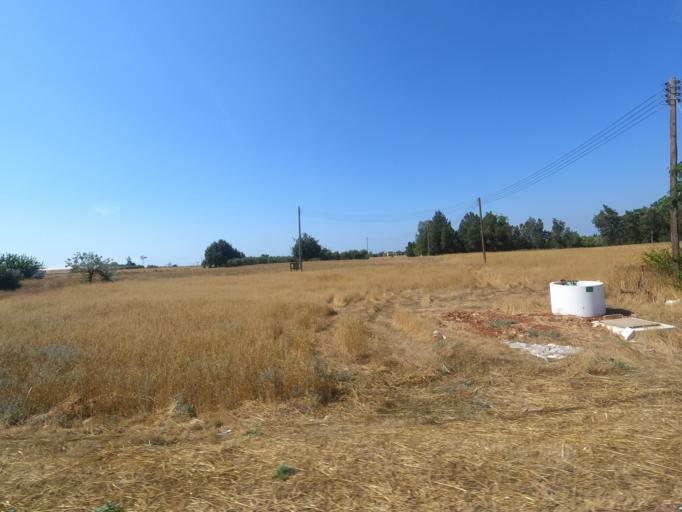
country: CY
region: Ammochostos
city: Frenaros
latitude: 35.0214
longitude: 33.9252
